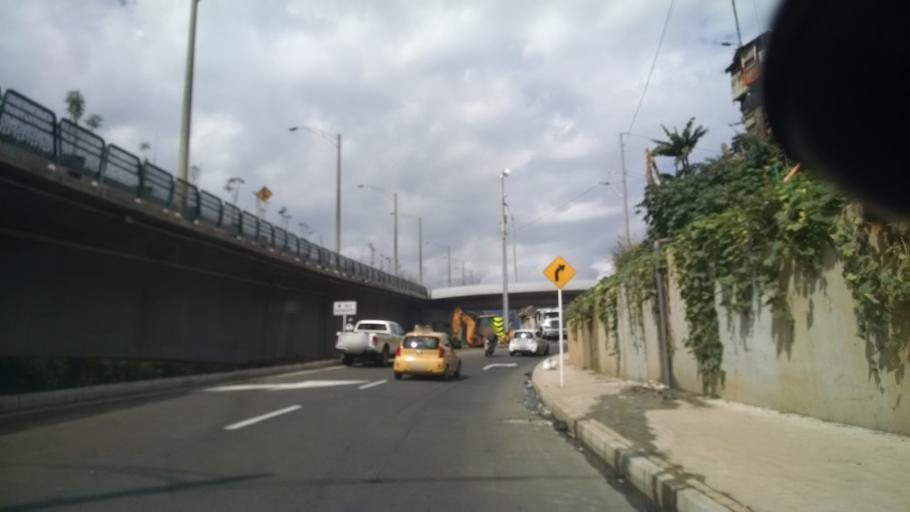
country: CO
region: Antioquia
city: Medellin
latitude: 6.2831
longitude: -75.5679
